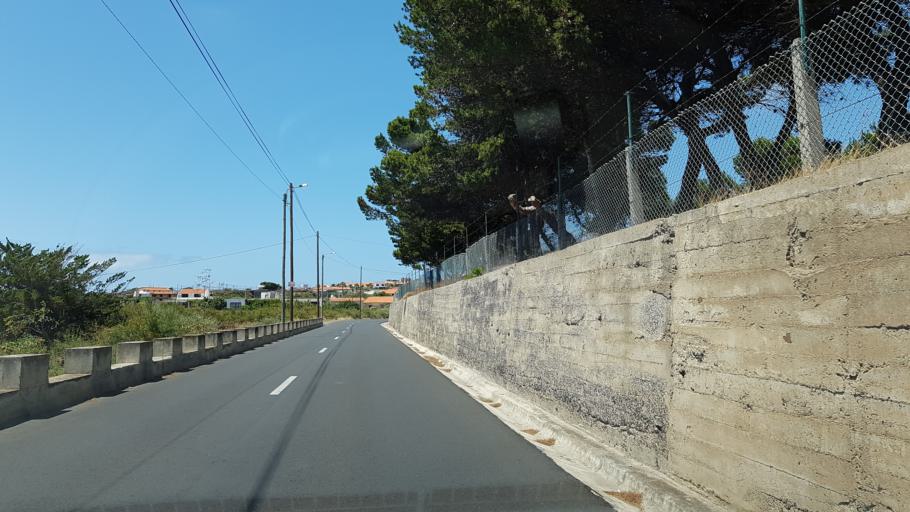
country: PT
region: Madeira
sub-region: Porto Santo
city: Camacha
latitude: 33.0769
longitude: -16.3461
